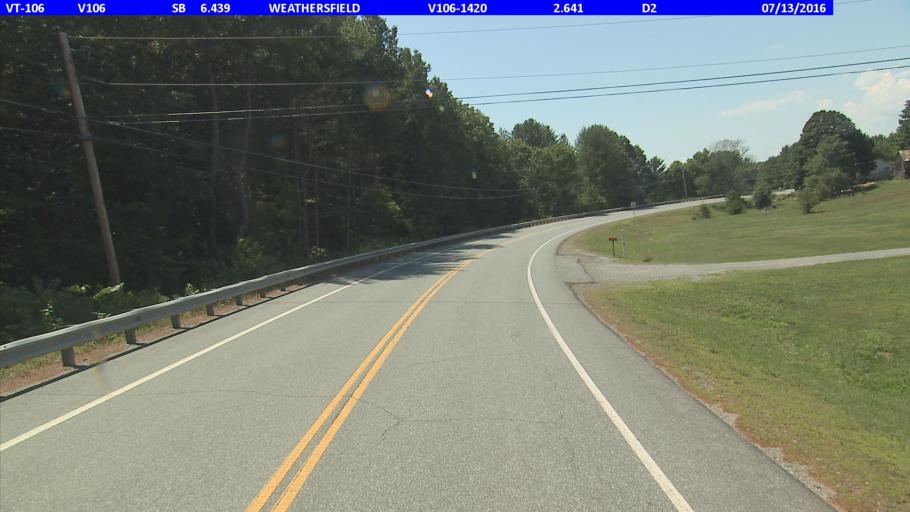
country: US
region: Vermont
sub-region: Windsor County
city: Springfield
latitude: 43.3773
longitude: -72.5085
